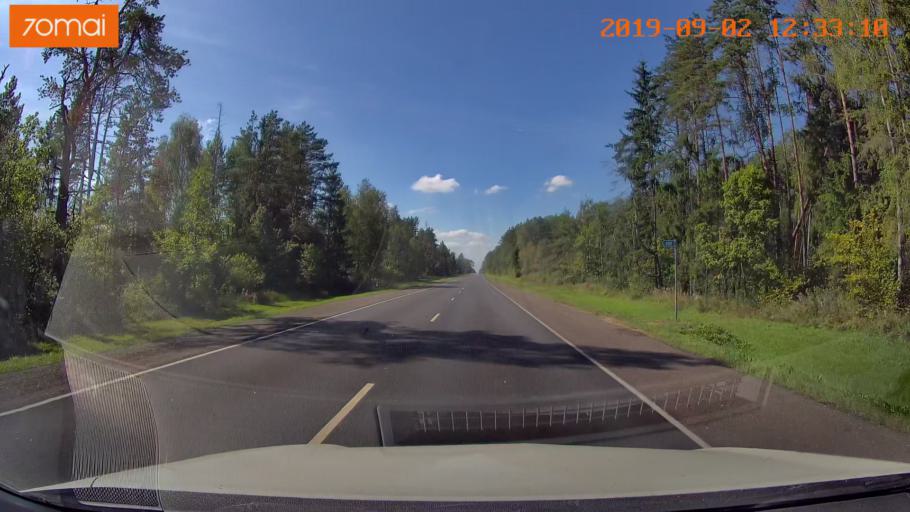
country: RU
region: Smolensk
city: Shumyachi
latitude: 53.8198
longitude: 32.4350
